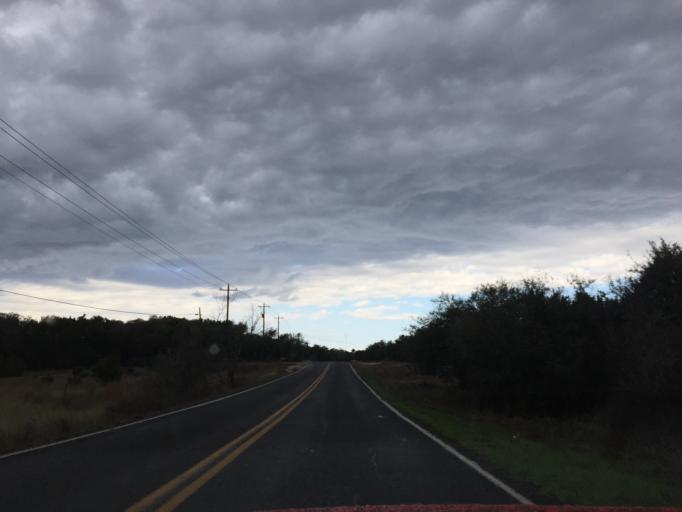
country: US
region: Texas
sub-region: Williamson County
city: Leander
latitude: 30.6091
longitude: -97.9343
